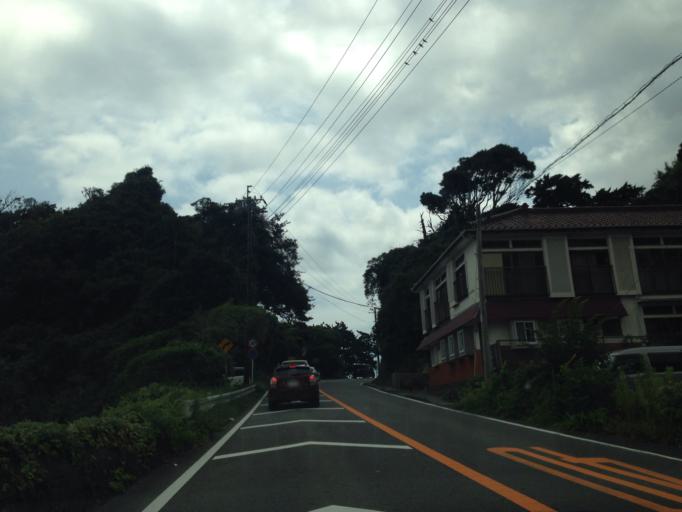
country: JP
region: Shizuoka
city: Shimoda
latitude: 34.7061
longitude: 138.9781
